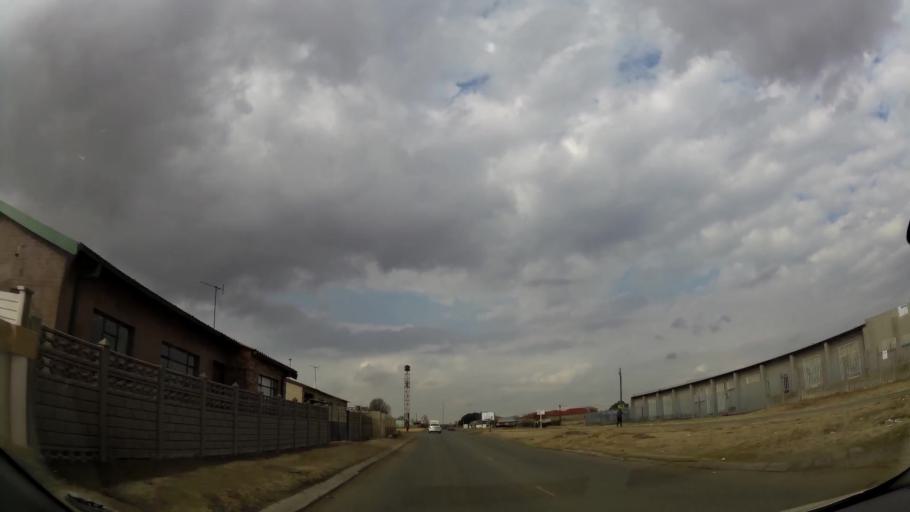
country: ZA
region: Orange Free State
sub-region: Fezile Dabi District Municipality
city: Sasolburg
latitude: -26.8415
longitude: 27.8462
